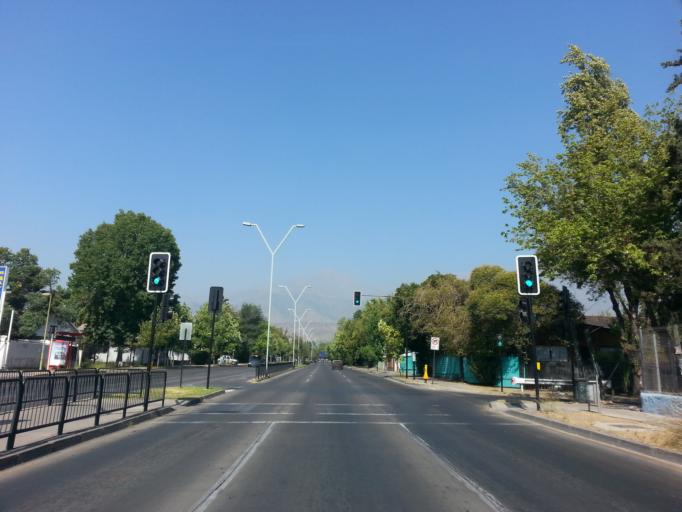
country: CL
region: Santiago Metropolitan
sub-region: Provincia de Santiago
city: Villa Presidente Frei, Nunoa, Santiago, Chile
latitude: -33.4309
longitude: -70.5602
